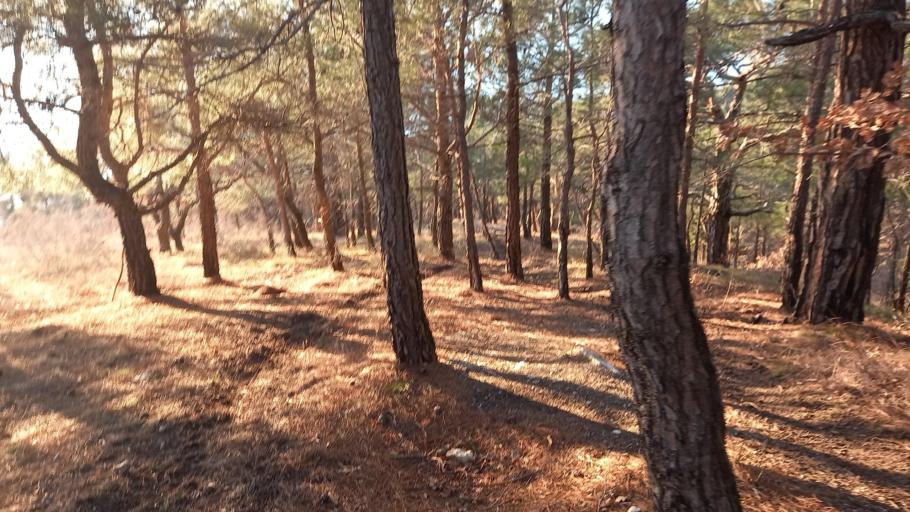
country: RU
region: Krasnodarskiy
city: Kabardinka
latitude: 44.6153
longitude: 37.9211
